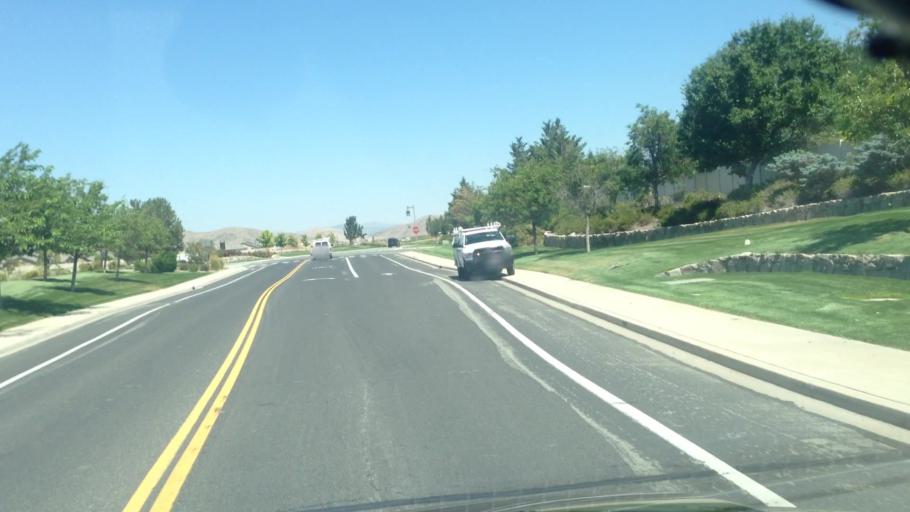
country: US
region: Nevada
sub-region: Washoe County
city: Sparks
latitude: 39.4307
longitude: -119.7168
